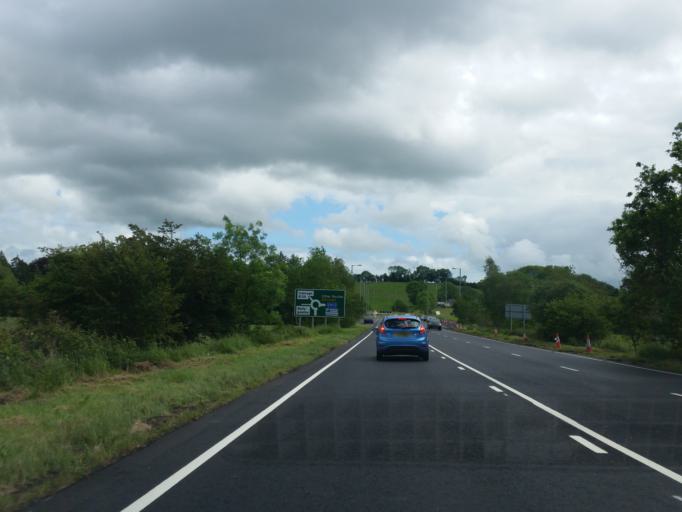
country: IE
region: Ulster
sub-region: County Monaghan
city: Monaghan
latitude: 54.4603
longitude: -7.0351
